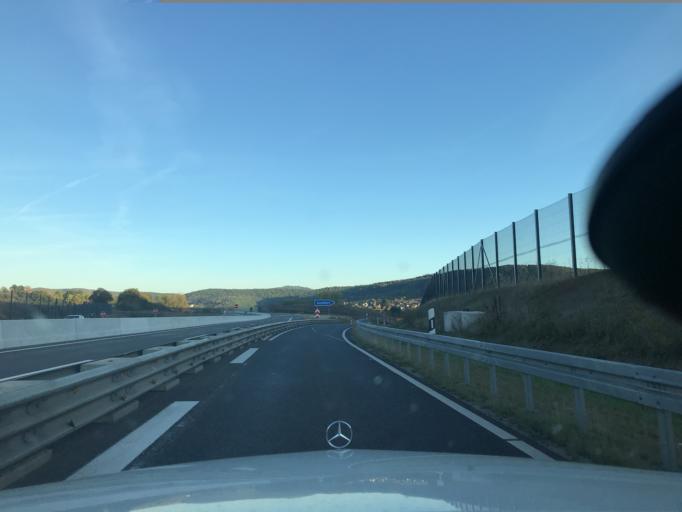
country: DE
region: Hesse
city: Waldkappel
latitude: 51.1472
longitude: 9.9196
